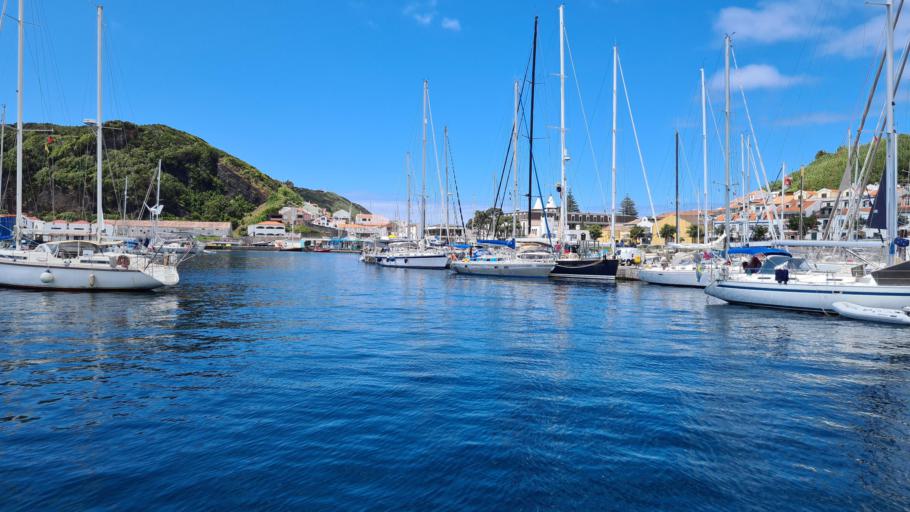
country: PT
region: Azores
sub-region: Horta
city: Horta
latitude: 38.5307
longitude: -28.6248
